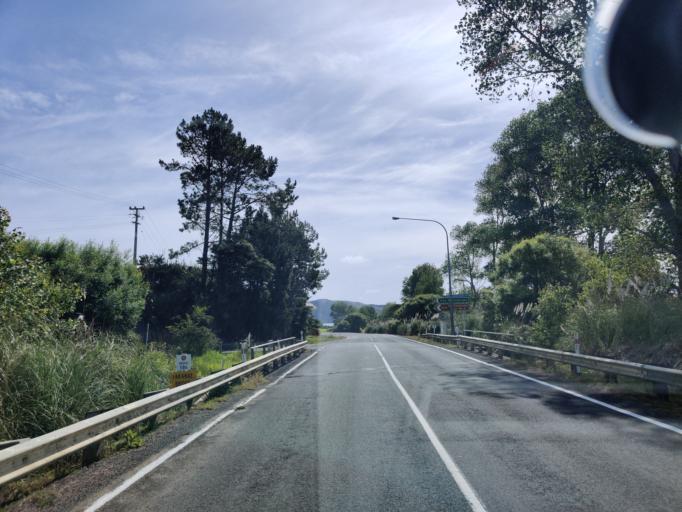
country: NZ
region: Northland
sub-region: Far North District
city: Kaitaia
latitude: -35.4959
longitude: 173.4133
